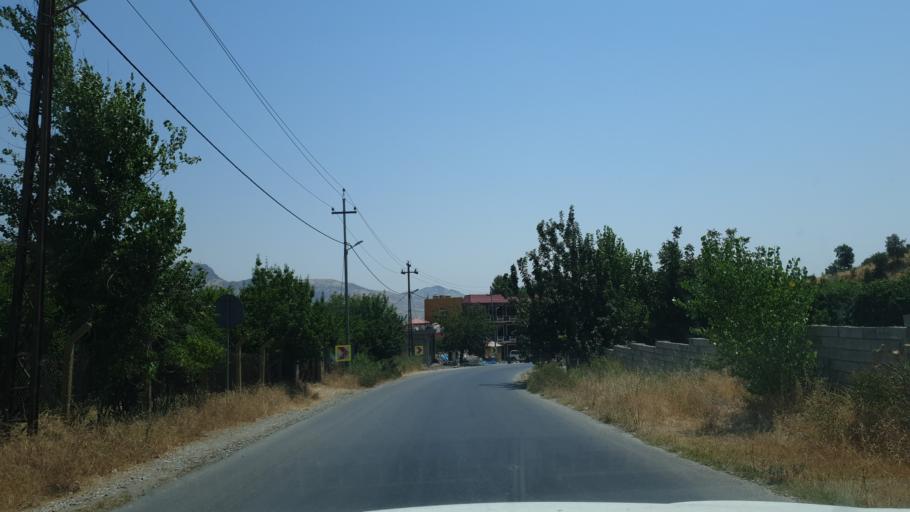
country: IQ
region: Arbil
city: Nahiyat Hiran
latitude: 36.2906
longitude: 44.4806
